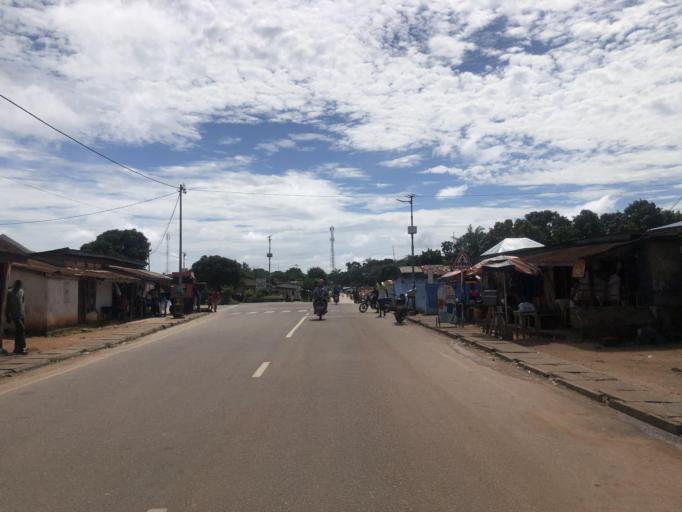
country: SL
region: Eastern Province
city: Koidu
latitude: 8.6386
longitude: -10.9721
